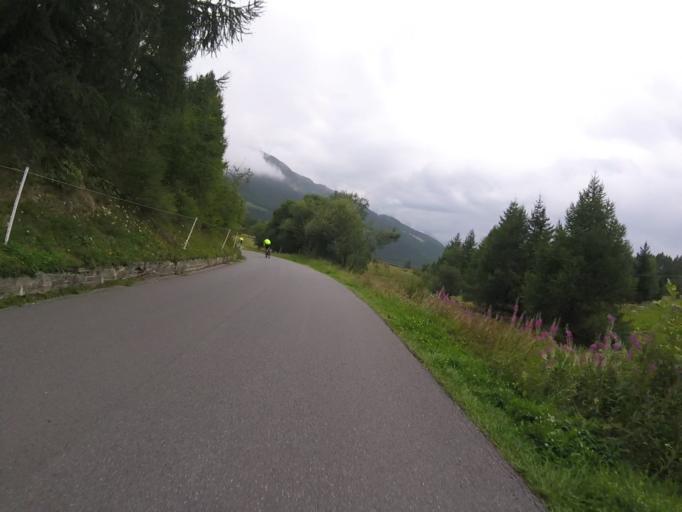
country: IT
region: Lombardy
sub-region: Provincia di Brescia
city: Monno
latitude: 46.2499
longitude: 10.3112
